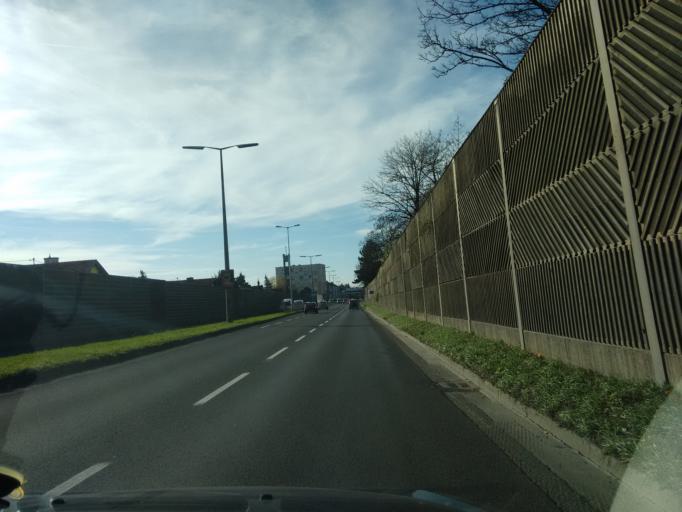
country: AT
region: Upper Austria
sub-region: Politischer Bezirk Linz-Land
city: Leonding
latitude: 48.2575
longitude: 14.2912
